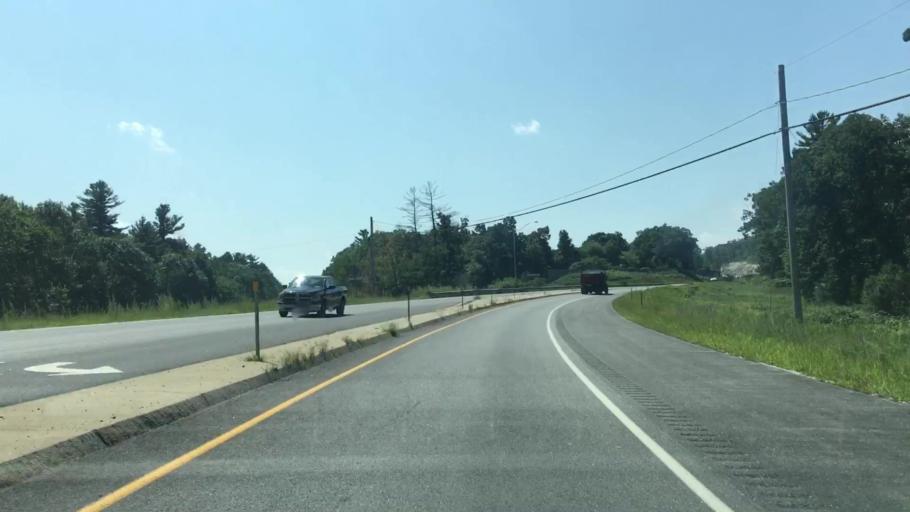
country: US
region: New Hampshire
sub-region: Rockingham County
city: Salem
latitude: 42.8350
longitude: -71.2320
